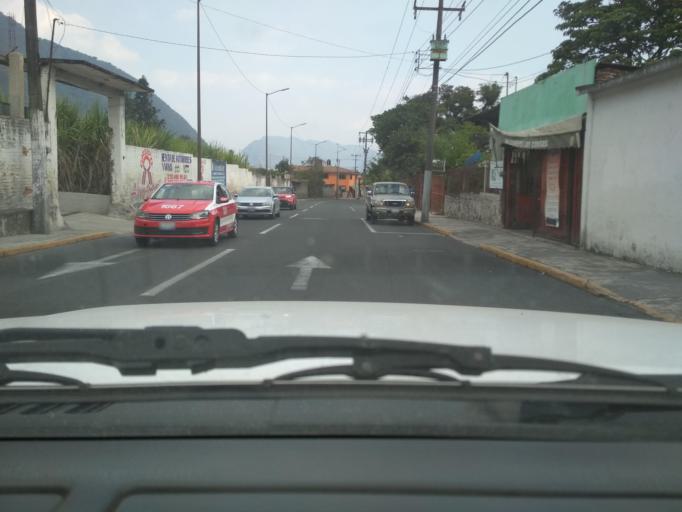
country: MX
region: Veracruz
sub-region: Mariano Escobedo
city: Palmira
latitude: 18.8714
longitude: -97.1026
